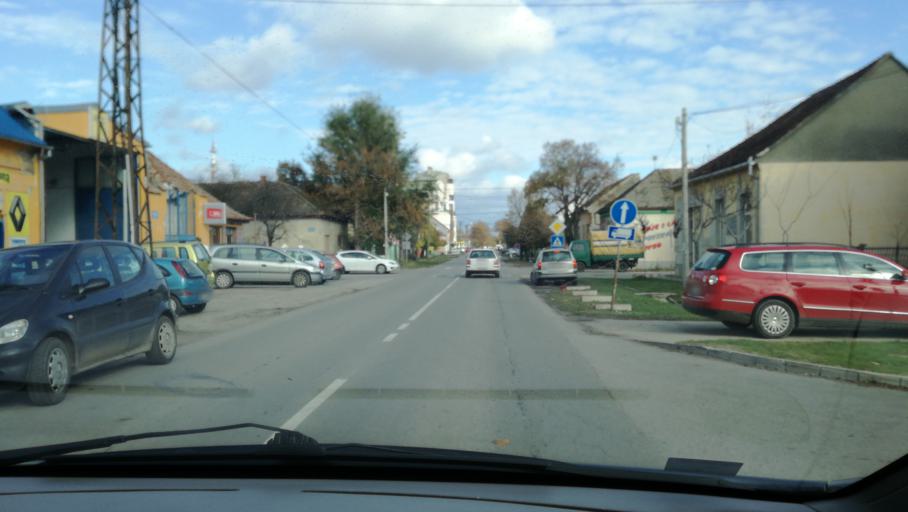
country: RS
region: Autonomna Pokrajina Vojvodina
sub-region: Severnobanatski Okrug
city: Kikinda
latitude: 45.8258
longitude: 20.4653
